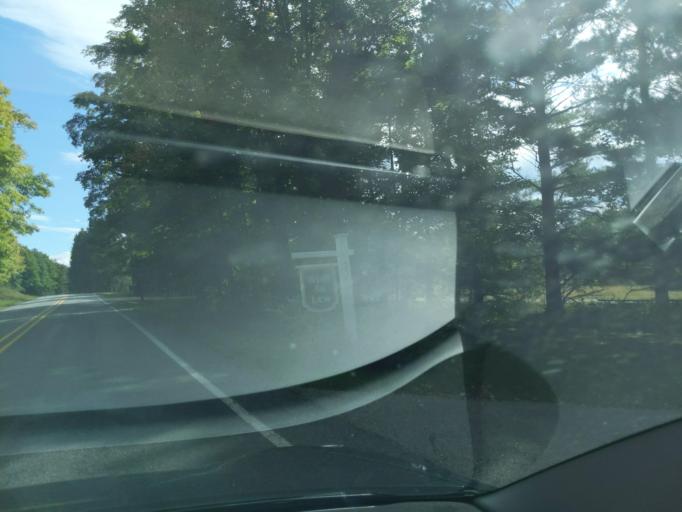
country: US
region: Michigan
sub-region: Antrim County
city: Bellaire
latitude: 44.9850
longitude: -85.2837
